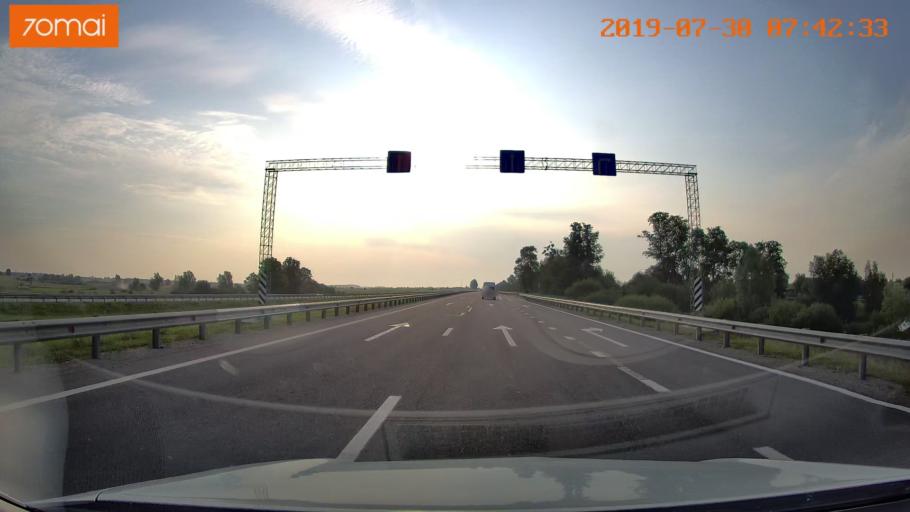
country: RU
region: Kaliningrad
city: Gvardeysk
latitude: 54.6479
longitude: 21.2821
